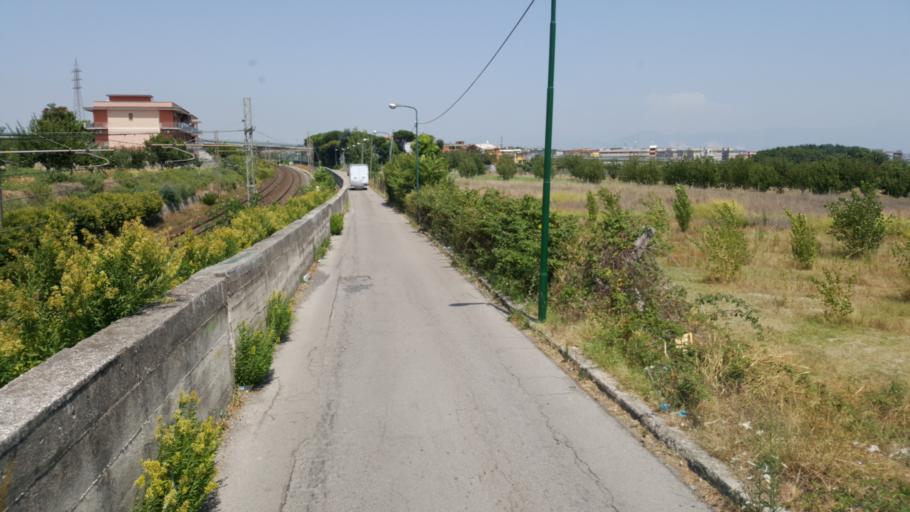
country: IT
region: Campania
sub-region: Provincia di Napoli
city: Arpino
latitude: 40.8845
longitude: 14.3134
